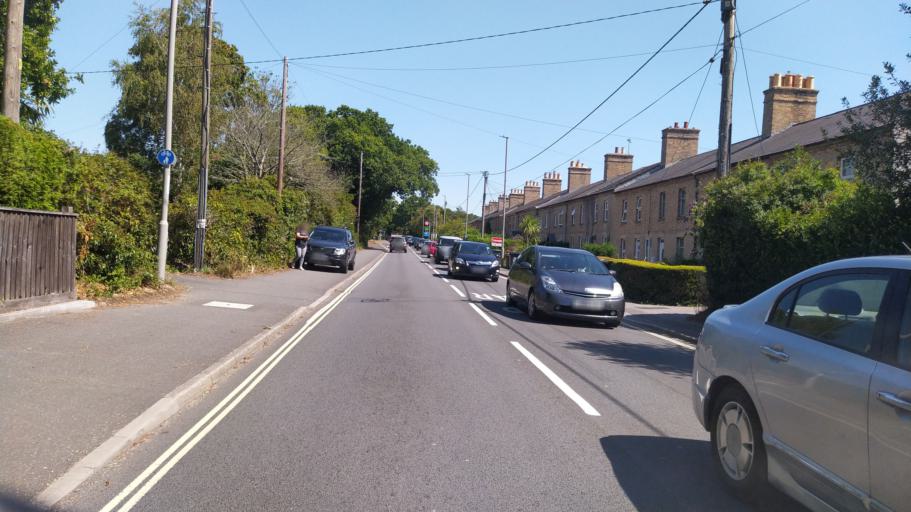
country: GB
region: England
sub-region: Dorset
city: Wareham
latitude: 50.7052
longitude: -2.1019
